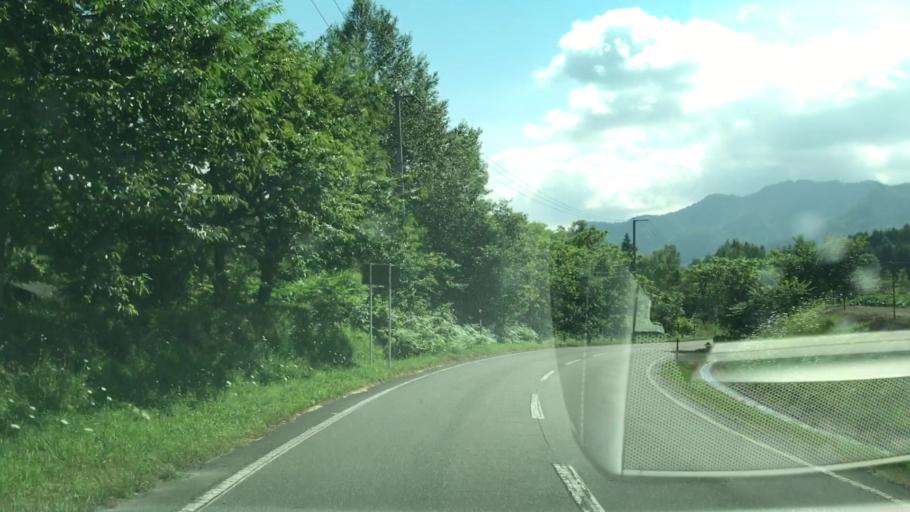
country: JP
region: Hokkaido
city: Shimo-furano
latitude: 42.8543
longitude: 142.4385
